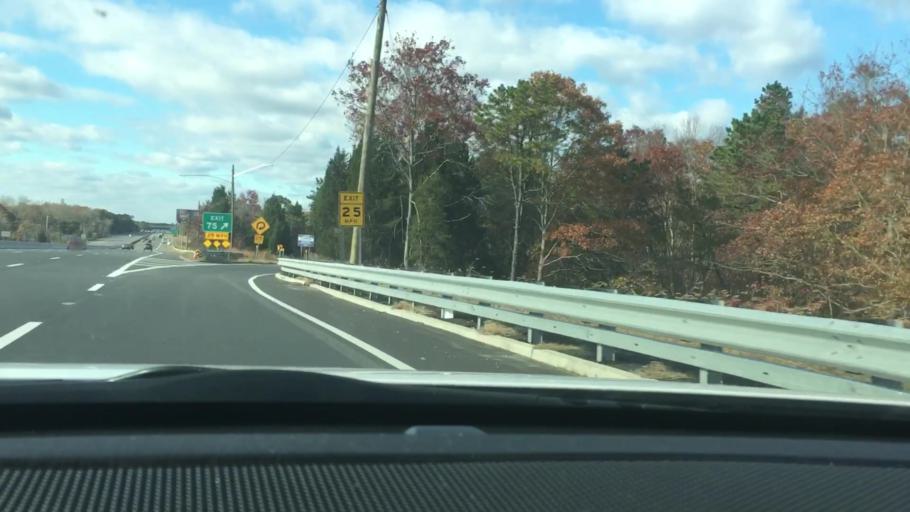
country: US
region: New Jersey
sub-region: Atlantic County
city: Pleasantville
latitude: 39.4142
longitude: -74.5539
